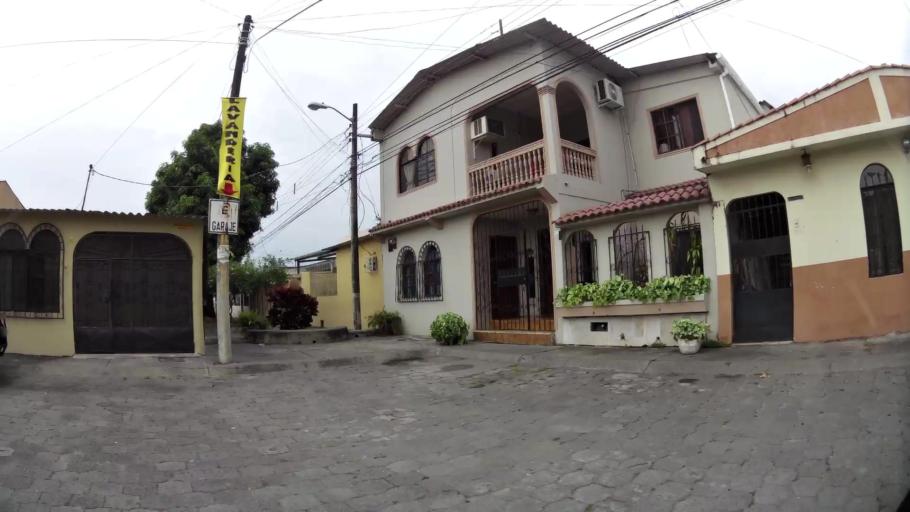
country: EC
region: Guayas
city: Eloy Alfaro
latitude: -2.1335
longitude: -79.8972
